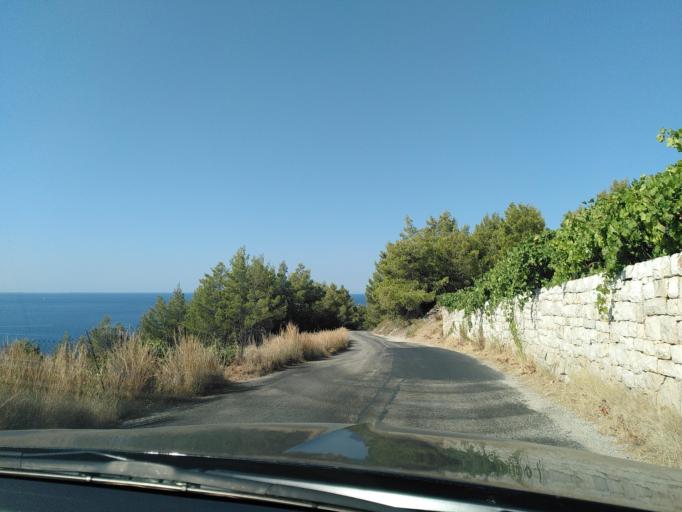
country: HR
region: Splitsko-Dalmatinska
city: Jelsa
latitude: 43.1240
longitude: 16.6732
